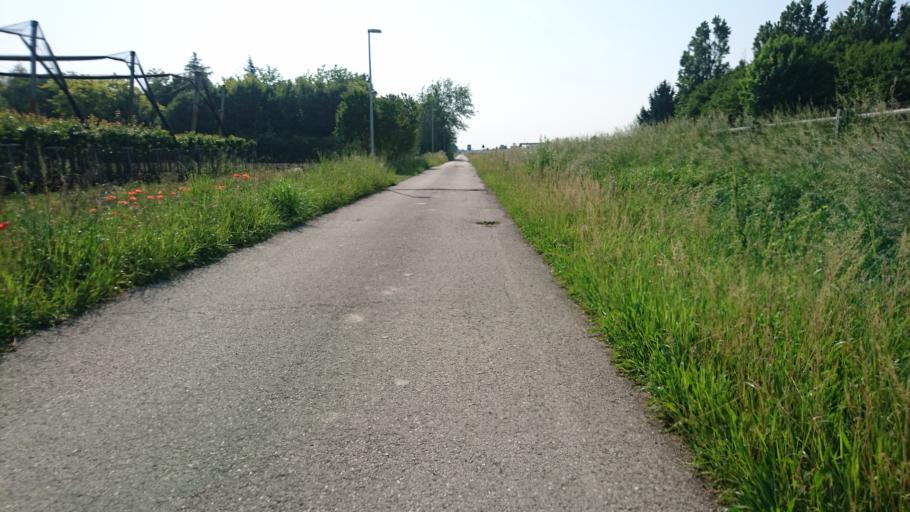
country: IT
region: Veneto
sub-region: Provincia di Padova
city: Villatora
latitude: 45.3780
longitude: 11.9778
